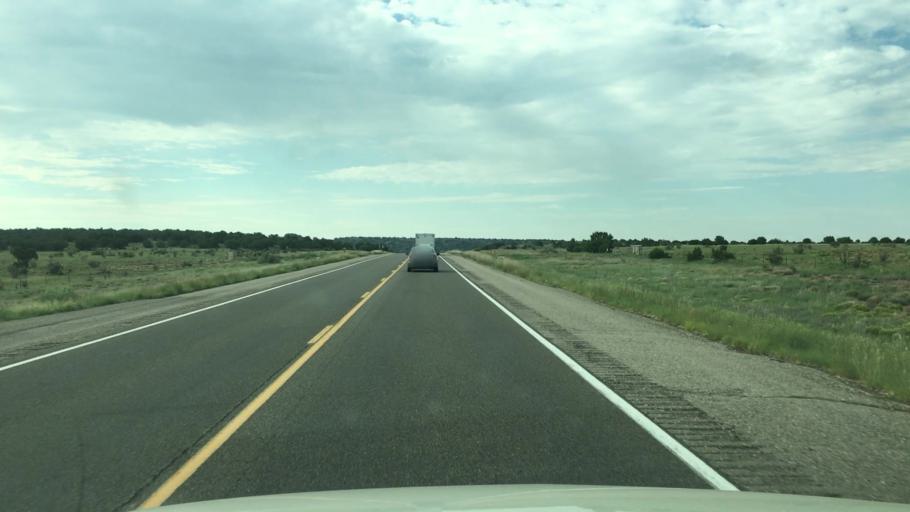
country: US
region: New Mexico
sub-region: Santa Fe County
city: Eldorado at Santa Fe
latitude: 35.2916
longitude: -105.8249
